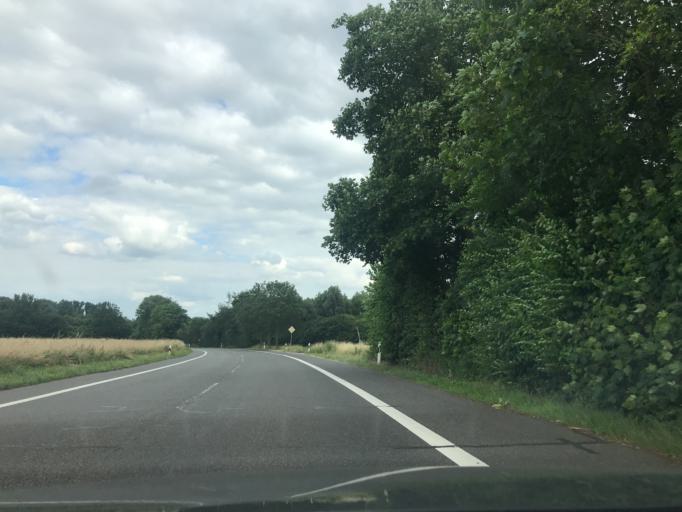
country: DE
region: North Rhine-Westphalia
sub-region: Regierungsbezirk Dusseldorf
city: Neubrueck
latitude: 51.1231
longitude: 6.7071
